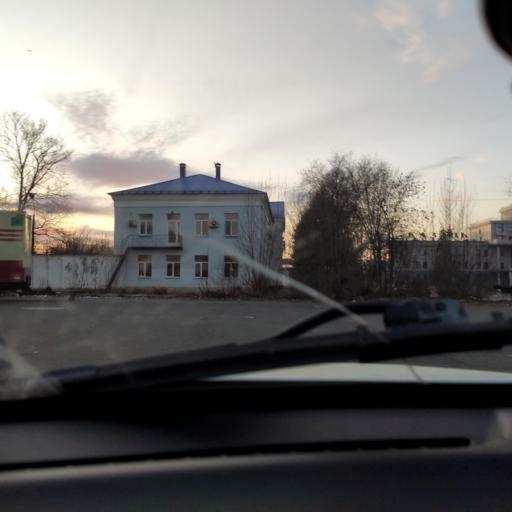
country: RU
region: Tatarstan
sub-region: Gorod Kazan'
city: Kazan
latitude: 55.7726
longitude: 49.0938
